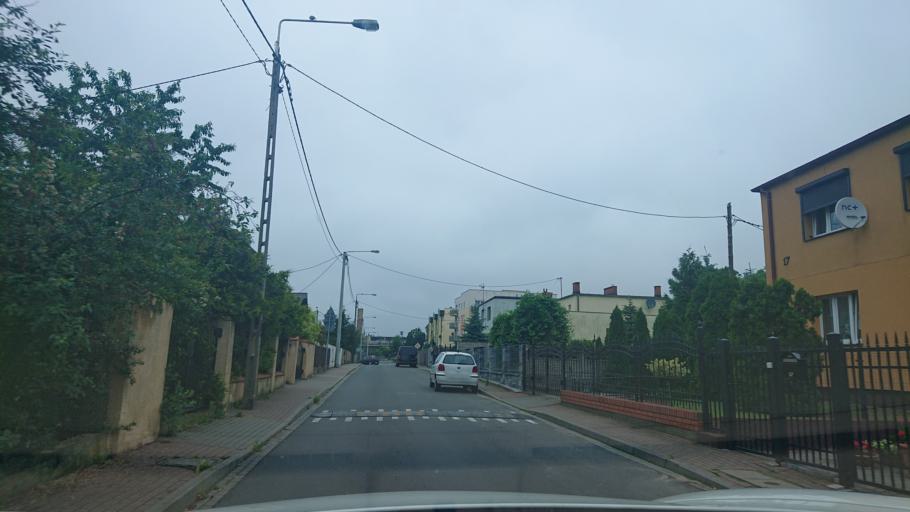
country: PL
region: Greater Poland Voivodeship
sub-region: Powiat gnieznienski
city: Gniezno
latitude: 52.5130
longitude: 17.6005
